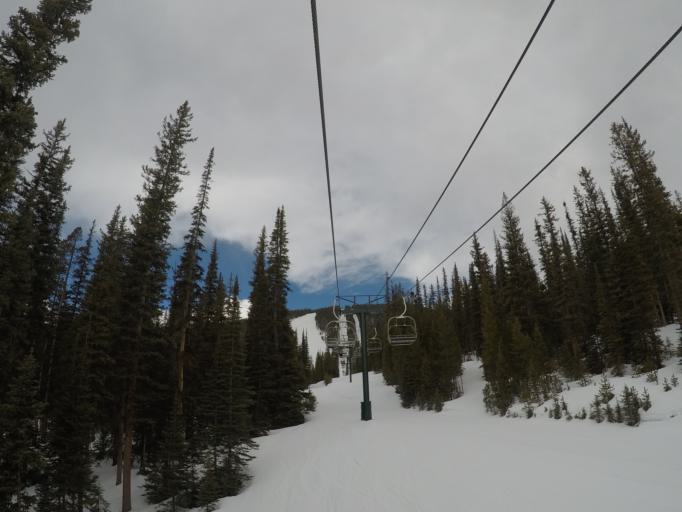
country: US
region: Montana
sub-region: Granite County
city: Philipsburg
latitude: 46.2511
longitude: -113.2410
